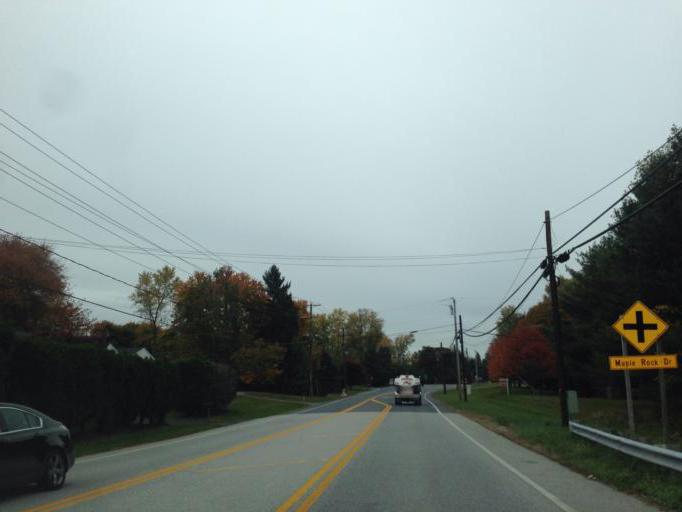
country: US
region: Maryland
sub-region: Howard County
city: Ellicott City
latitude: 39.3009
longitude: -76.8331
